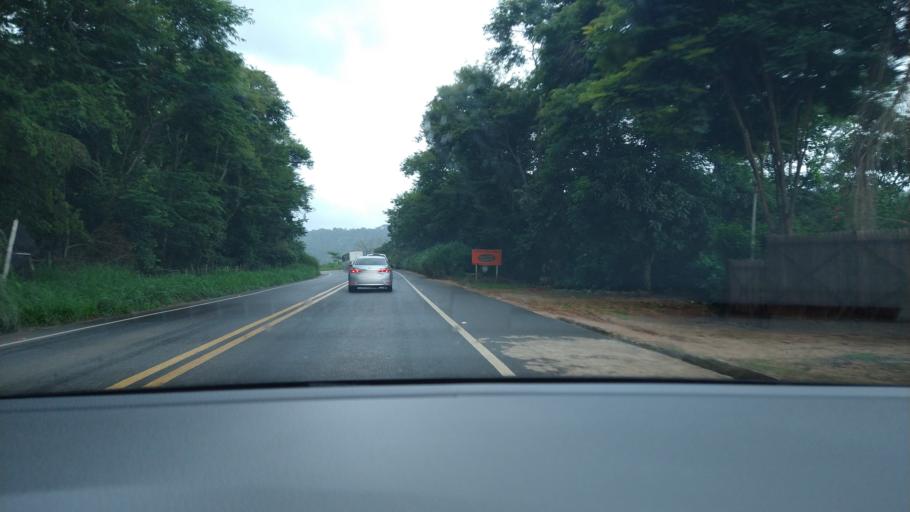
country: BR
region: Minas Gerais
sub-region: Vicosa
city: Vicosa
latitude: -20.6506
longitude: -42.8601
